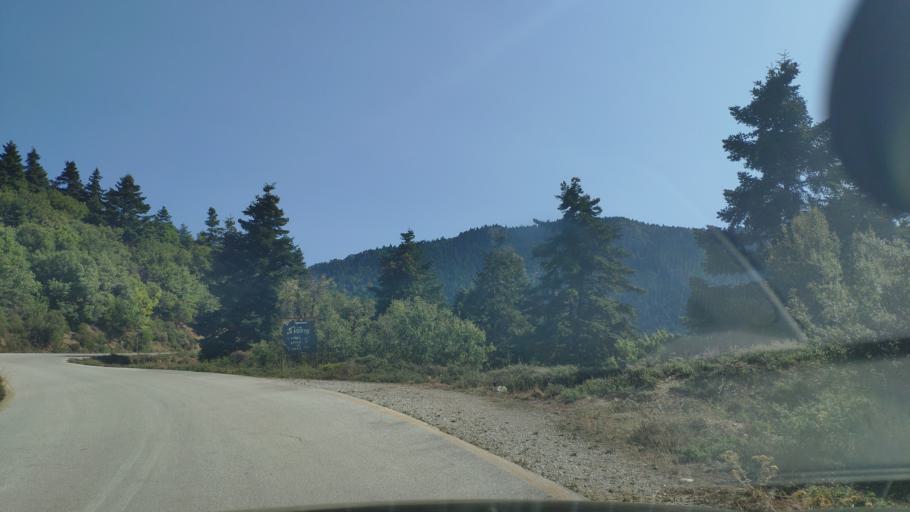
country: GR
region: Peloponnese
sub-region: Nomos Korinthias
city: Nemea
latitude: 37.8622
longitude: 22.3822
